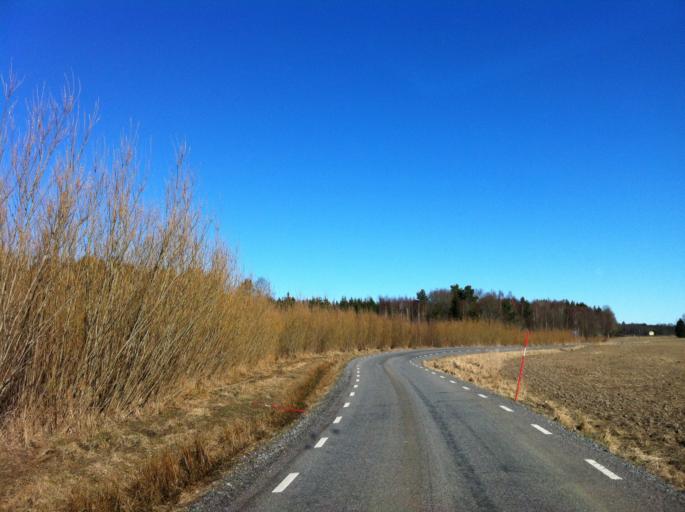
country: SE
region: Vaestra Goetaland
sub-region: Grastorps Kommun
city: Graestorp
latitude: 58.4344
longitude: 12.6078
